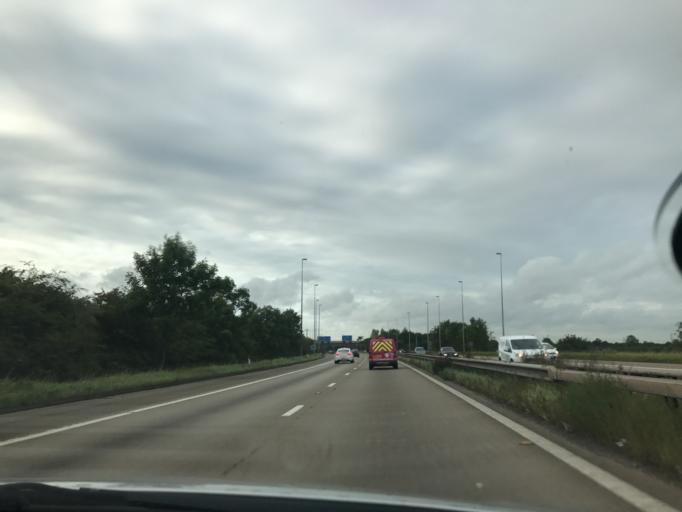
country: GB
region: England
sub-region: Cheshire West and Chester
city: Stoke
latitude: 53.2385
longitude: -2.8625
